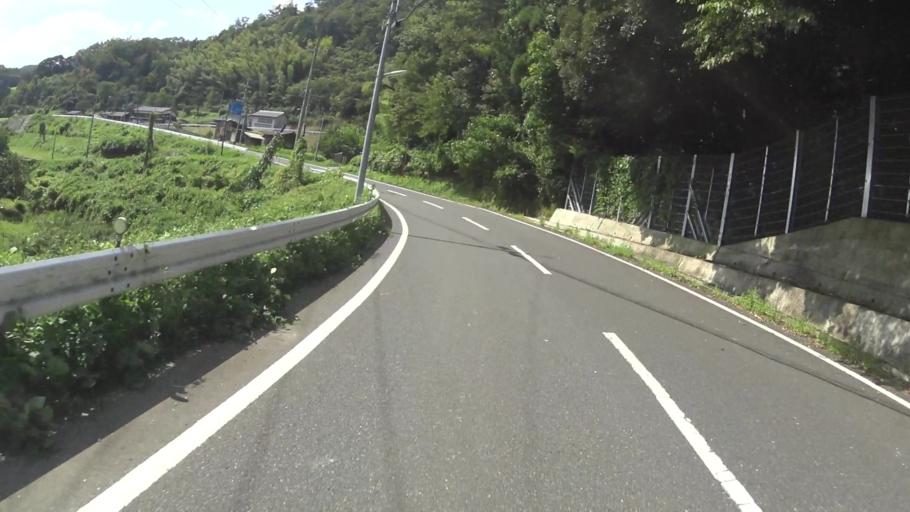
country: JP
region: Kyoto
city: Miyazu
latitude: 35.7049
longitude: 135.2518
